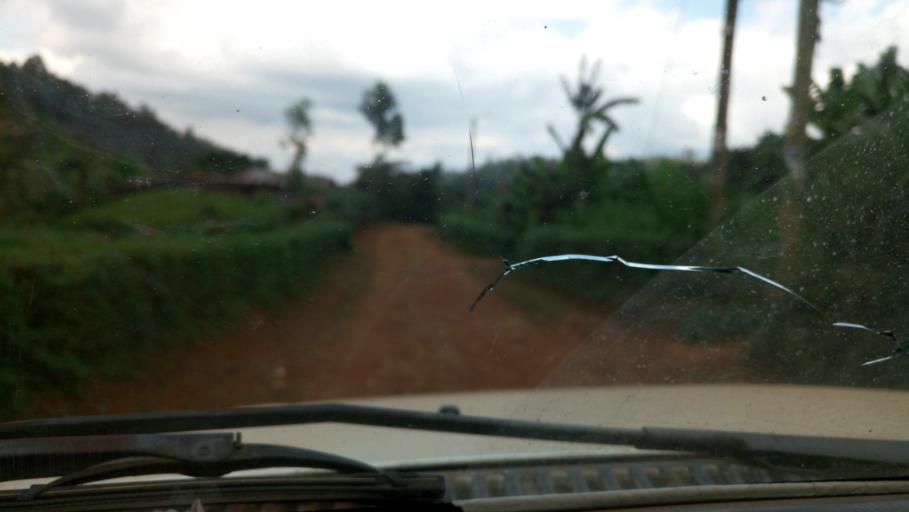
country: KE
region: Murang'a District
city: Kangema
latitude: -0.7805
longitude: 36.9319
